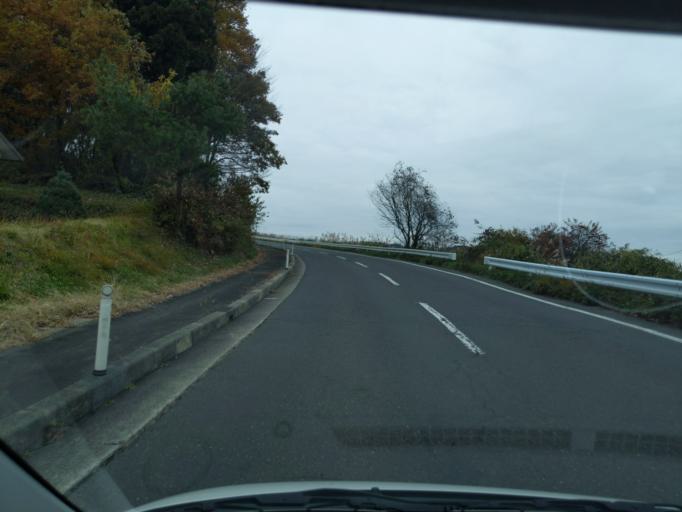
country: JP
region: Iwate
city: Mizusawa
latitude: 39.1987
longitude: 141.2222
